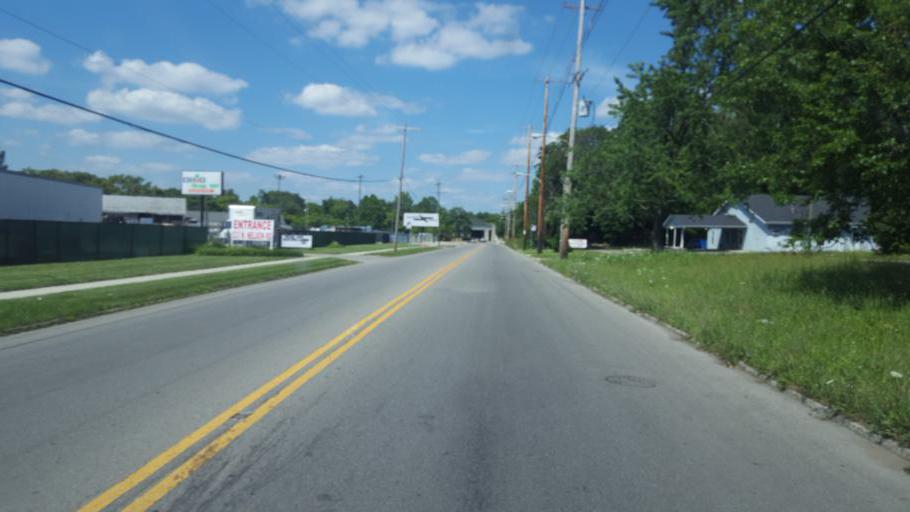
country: US
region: Ohio
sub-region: Franklin County
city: Bexley
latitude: 39.9786
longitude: -82.9451
